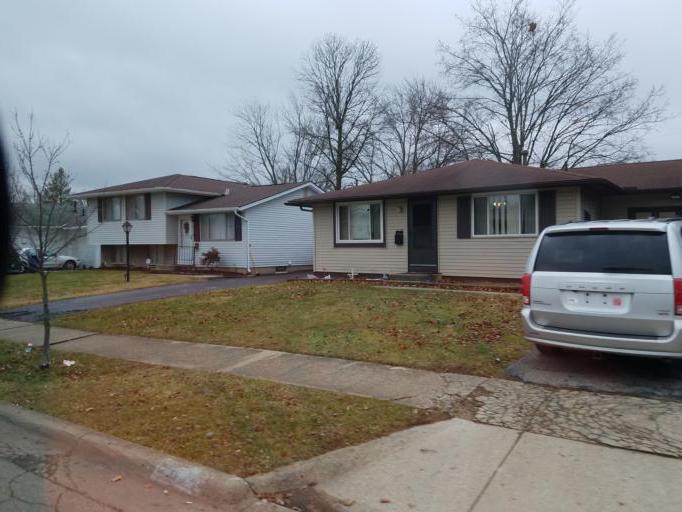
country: US
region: Ohio
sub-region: Franklin County
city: Minerva Park
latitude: 40.0839
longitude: -82.9631
